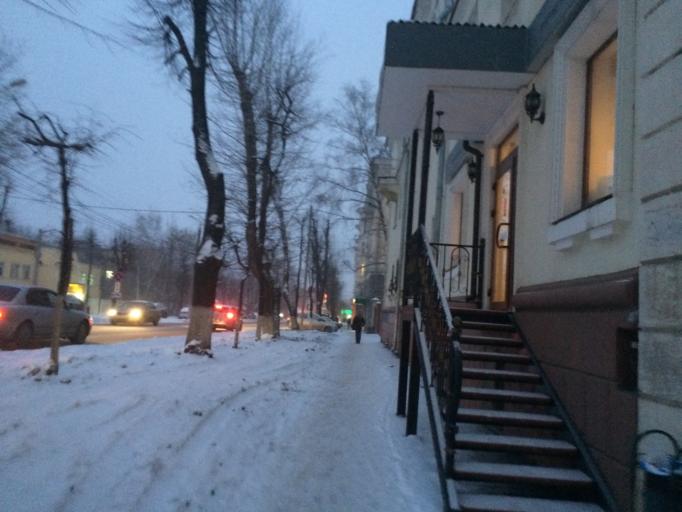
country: RU
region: Tula
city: Tula
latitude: 54.1808
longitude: 37.6002
